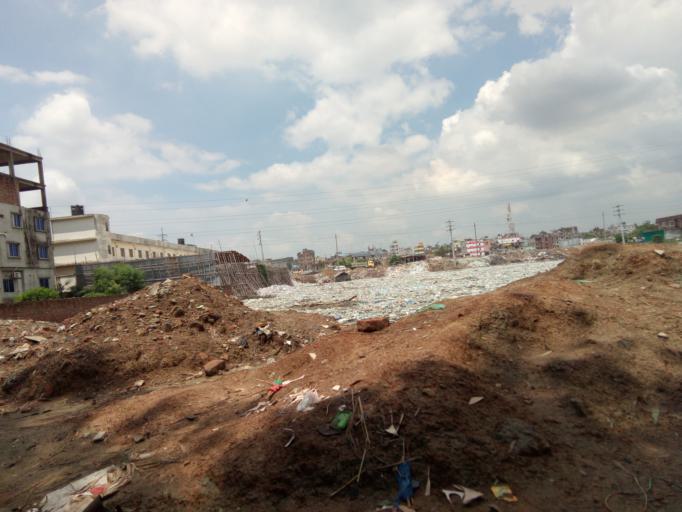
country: BD
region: Dhaka
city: Azimpur
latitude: 23.7302
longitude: 90.3625
